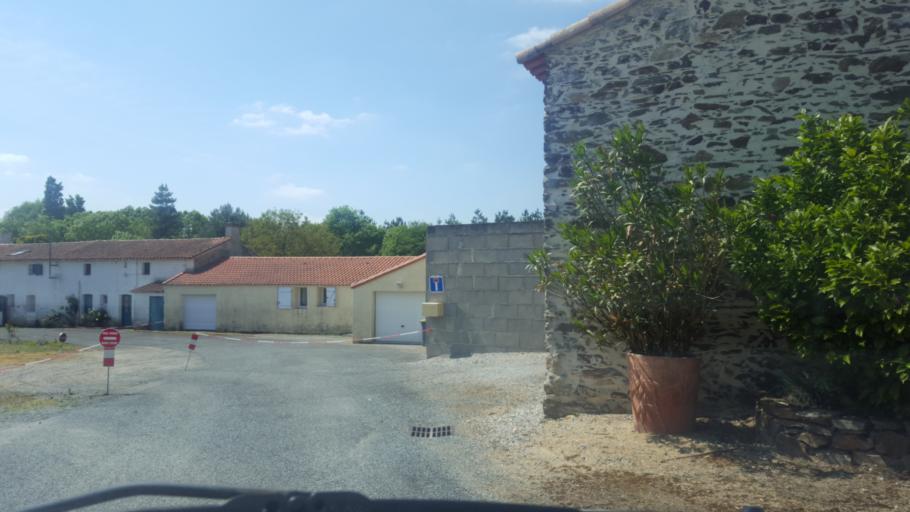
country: FR
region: Pays de la Loire
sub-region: Departement de la Loire-Atlantique
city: Saint-Philbert-de-Grand-Lieu
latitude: 47.0342
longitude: -1.6051
